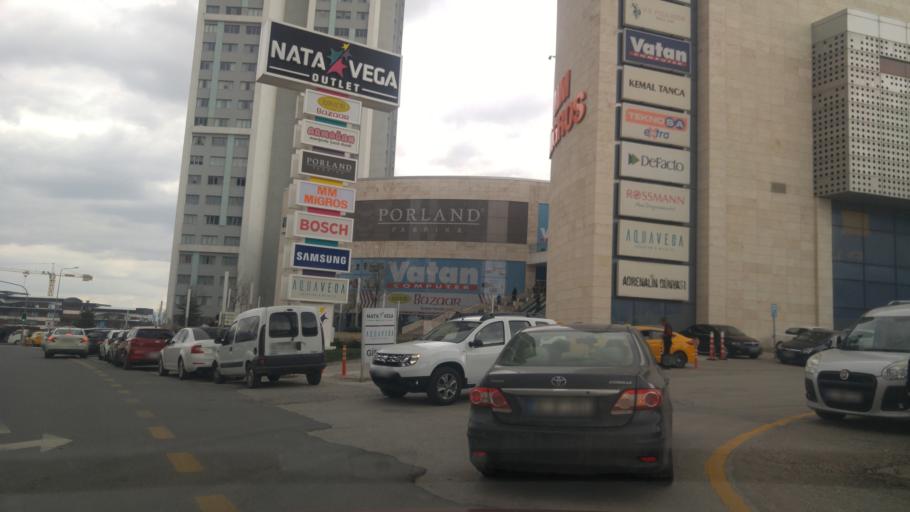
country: TR
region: Ankara
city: Mamak
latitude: 39.8895
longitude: 32.9328
